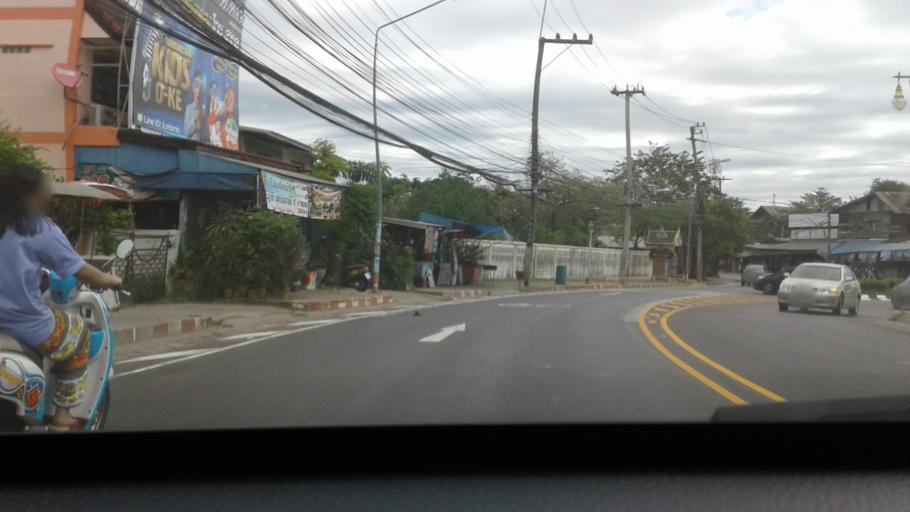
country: TH
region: Changwat Udon Thani
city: Udon Thani
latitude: 17.4213
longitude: 102.7839
